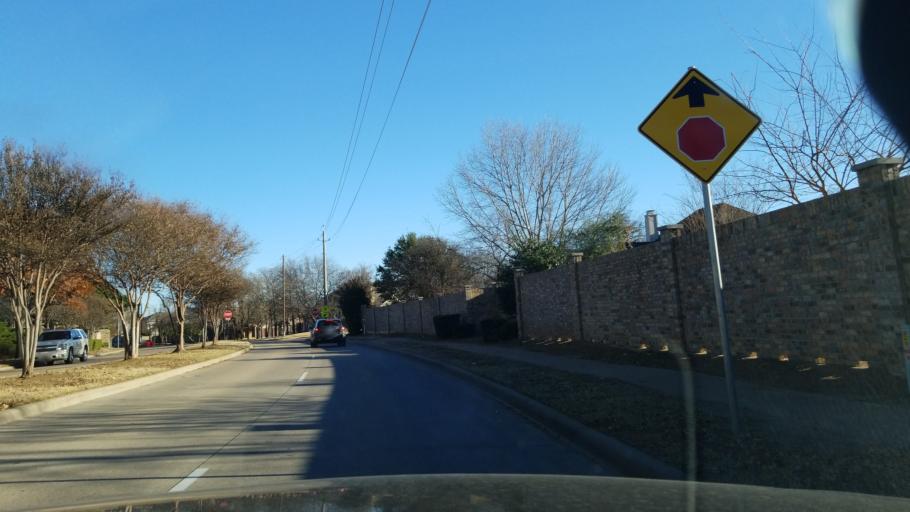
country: US
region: Texas
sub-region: Denton County
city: Corinth
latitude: 33.1557
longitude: -97.0857
